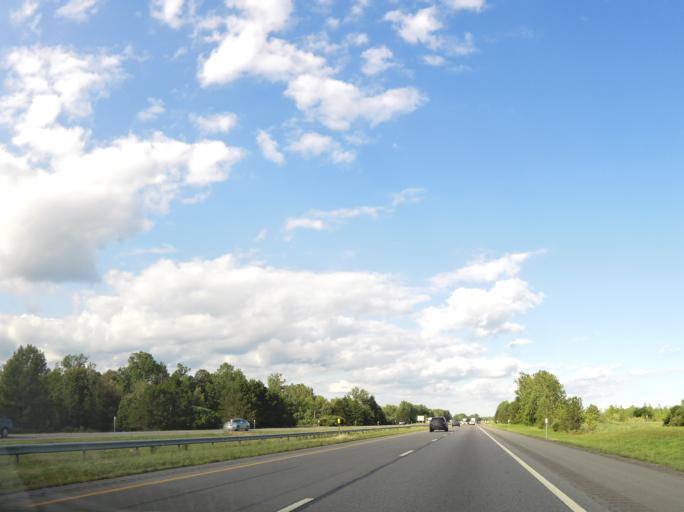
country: US
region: New York
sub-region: Erie County
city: Clarence
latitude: 42.9590
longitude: -78.5761
